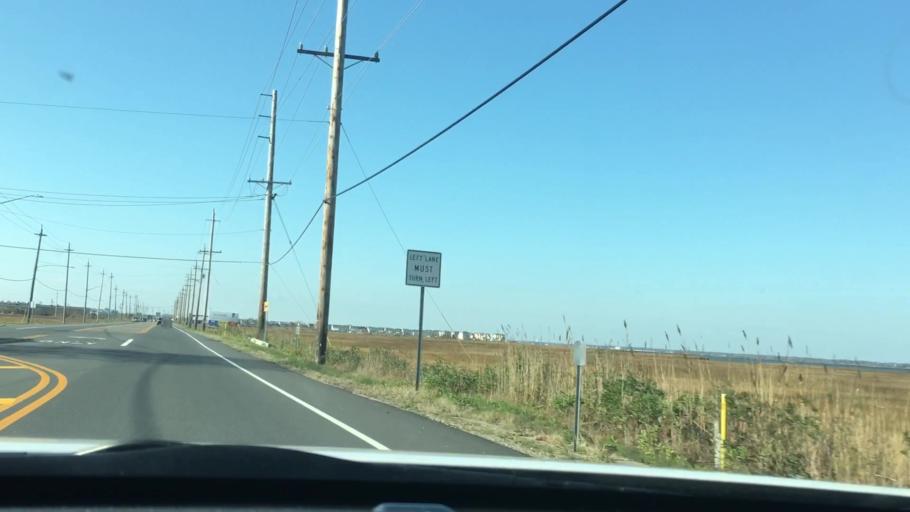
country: US
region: New Jersey
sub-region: Atlantic County
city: Ventnor City
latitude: 39.3577
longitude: -74.4678
